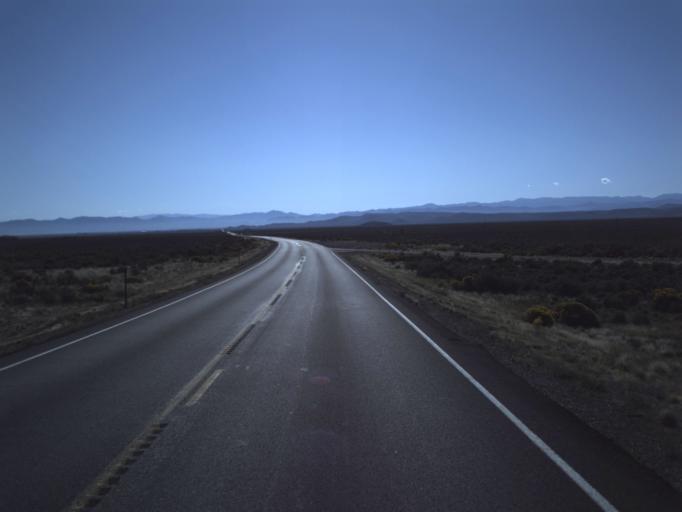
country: US
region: Utah
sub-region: Washington County
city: Enterprise
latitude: 37.7994
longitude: -113.9128
